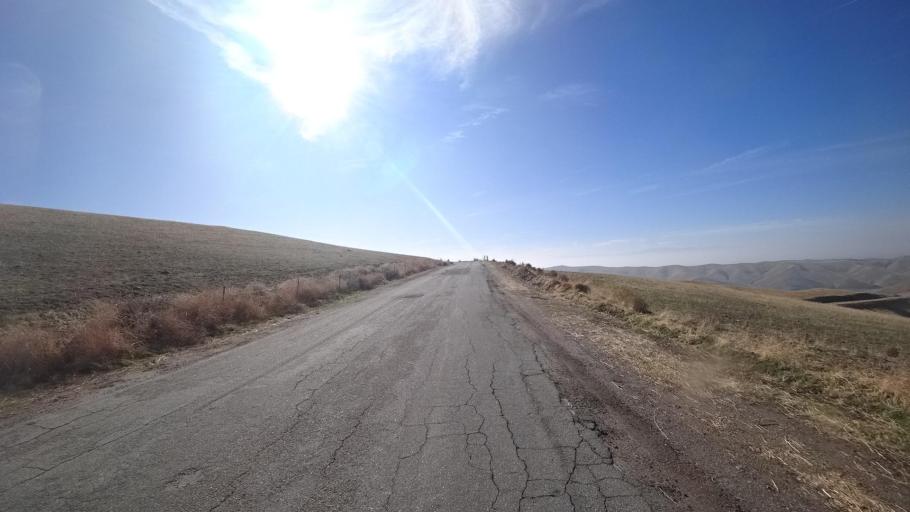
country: US
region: California
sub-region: Kern County
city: Arvin
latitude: 35.4015
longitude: -118.7727
